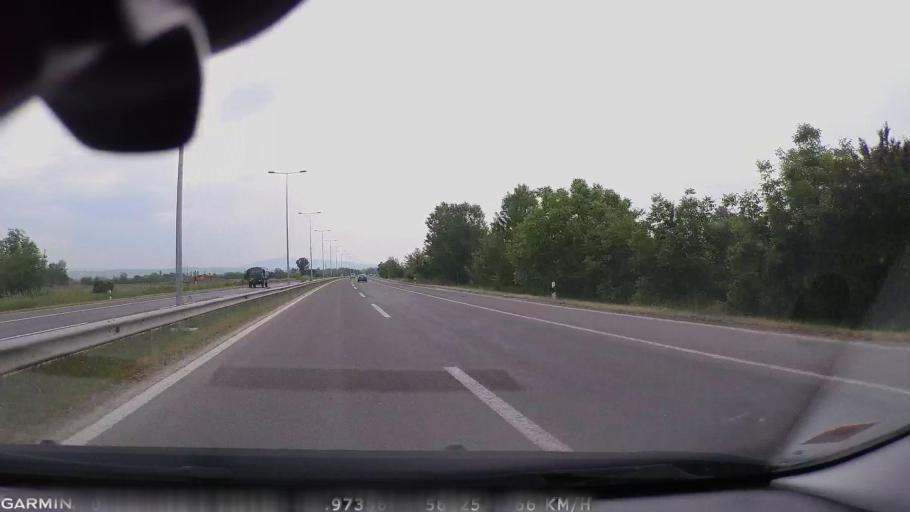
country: MK
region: Ilinden
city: Jurumleri
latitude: 41.9745
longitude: 21.5566
